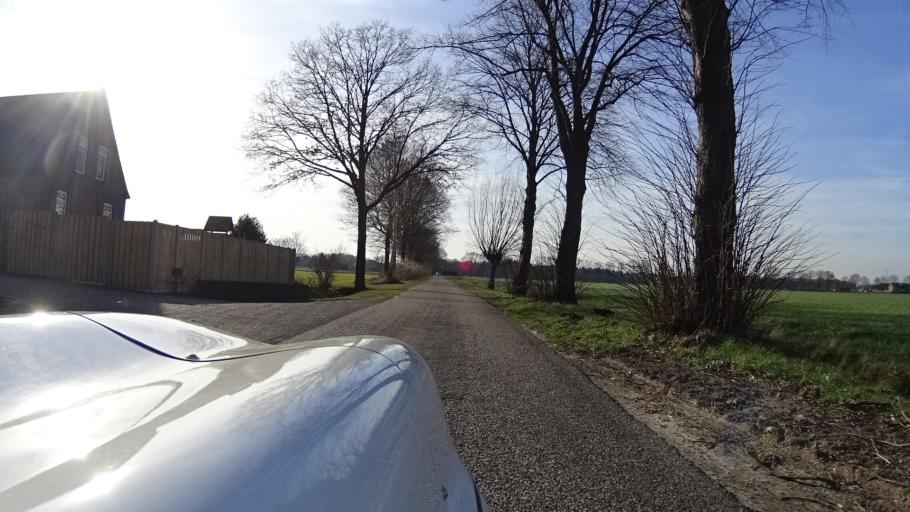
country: NL
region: North Brabant
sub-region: Gemeente Boekel
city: Boekel
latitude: 51.5782
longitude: 5.6629
